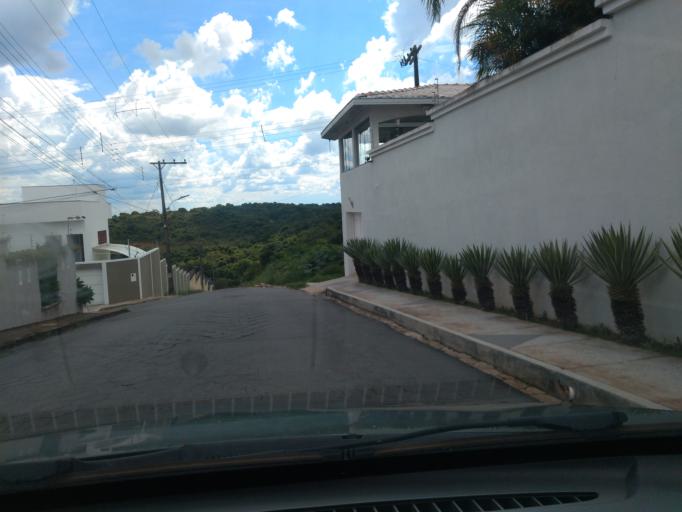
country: BR
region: Minas Gerais
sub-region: Tres Coracoes
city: Tres Coracoes
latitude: -21.6921
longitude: -45.2640
